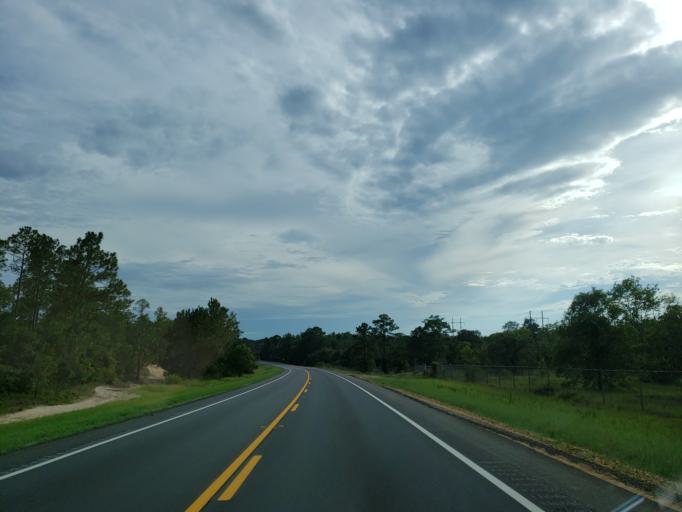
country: US
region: Georgia
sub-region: Berrien County
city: Enigma
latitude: 31.5367
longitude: -83.3943
